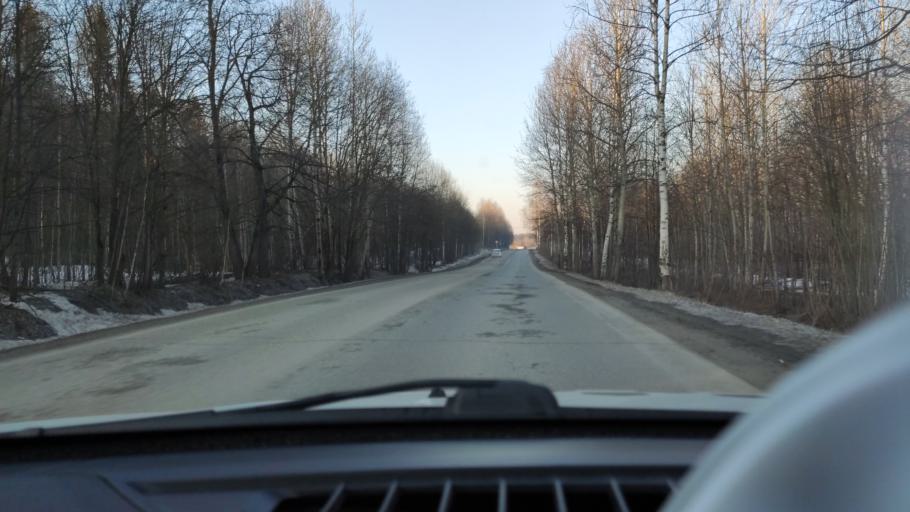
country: RU
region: Perm
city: Perm
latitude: 58.0996
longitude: 56.4093
